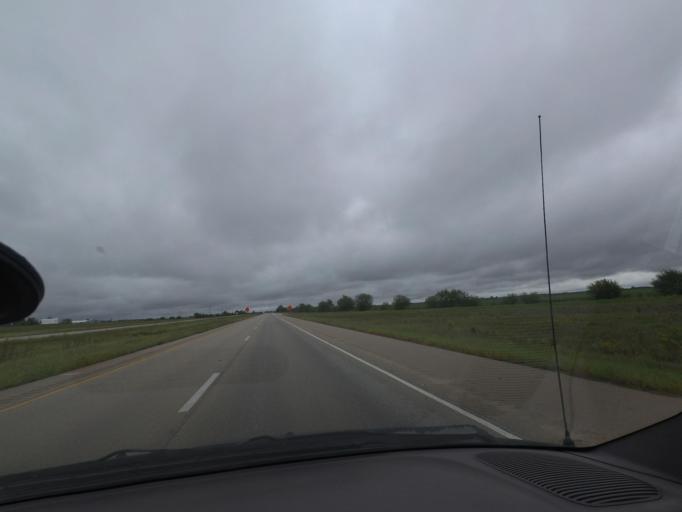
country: US
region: Illinois
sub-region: Piatt County
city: Cerro Gordo
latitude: 39.9560
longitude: -88.8218
